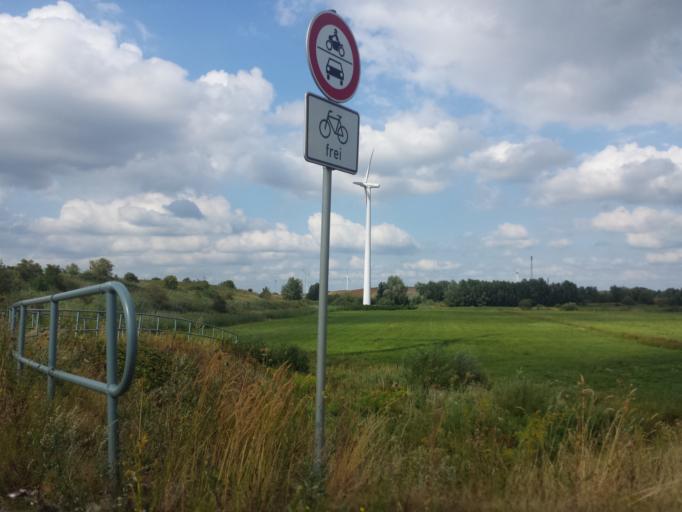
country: DE
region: Lower Saxony
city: Delmenhorst
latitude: 53.0975
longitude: 8.6937
